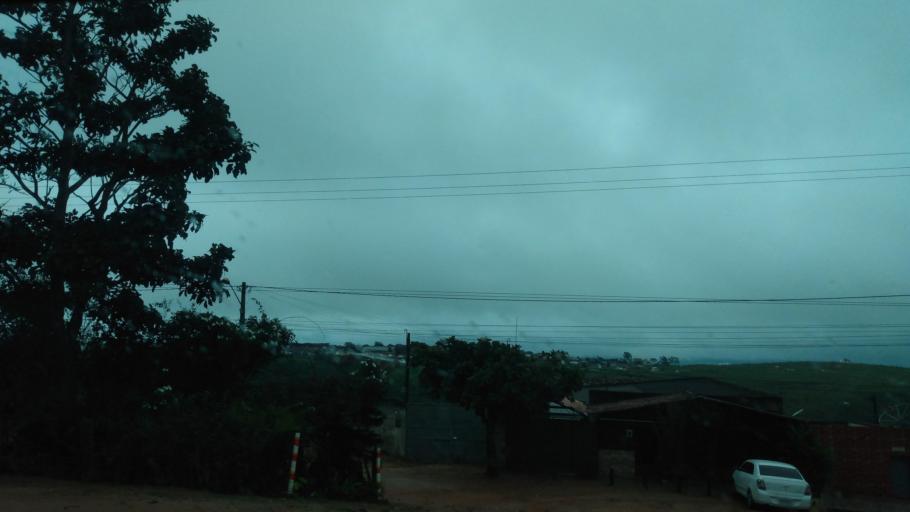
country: BR
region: Pernambuco
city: Garanhuns
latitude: -8.8775
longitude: -36.4995
